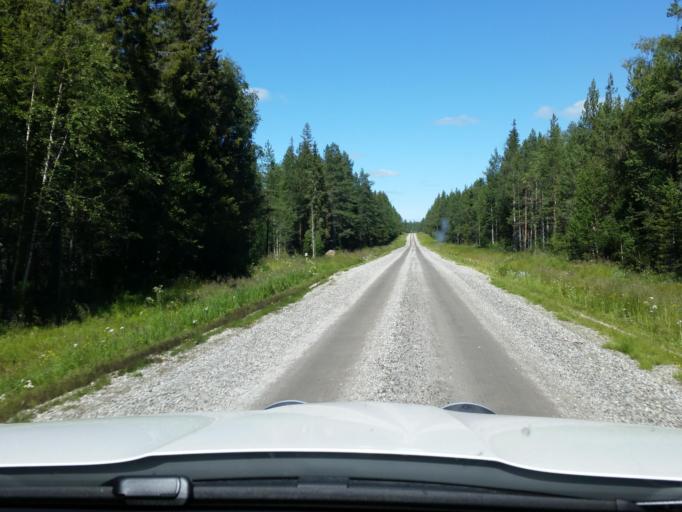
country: SE
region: Vaesterbotten
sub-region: Skelleftea Kommun
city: Storvik
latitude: 65.2916
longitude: 20.6561
